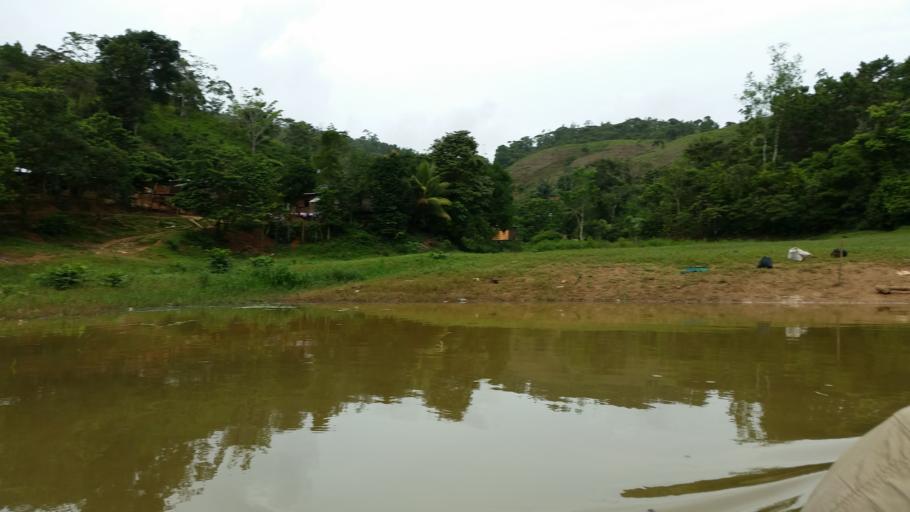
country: NI
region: Atlantico Norte (RAAN)
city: Bonanza
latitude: 13.9762
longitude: -84.6977
